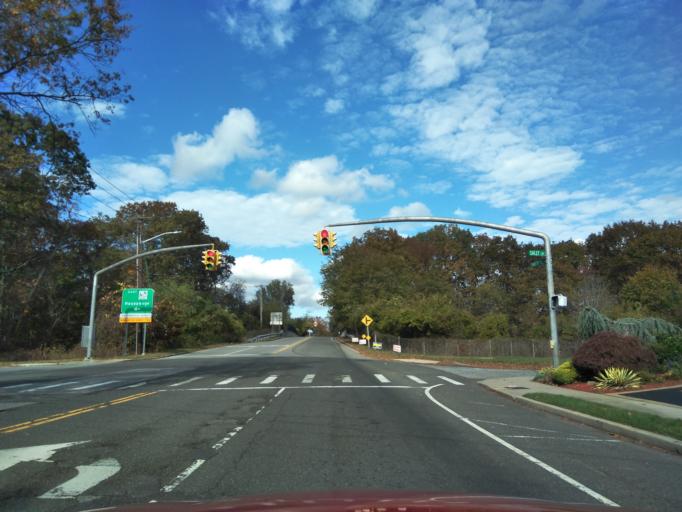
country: US
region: New York
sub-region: Nassau County
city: Plainview
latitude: 40.7946
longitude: -73.4791
